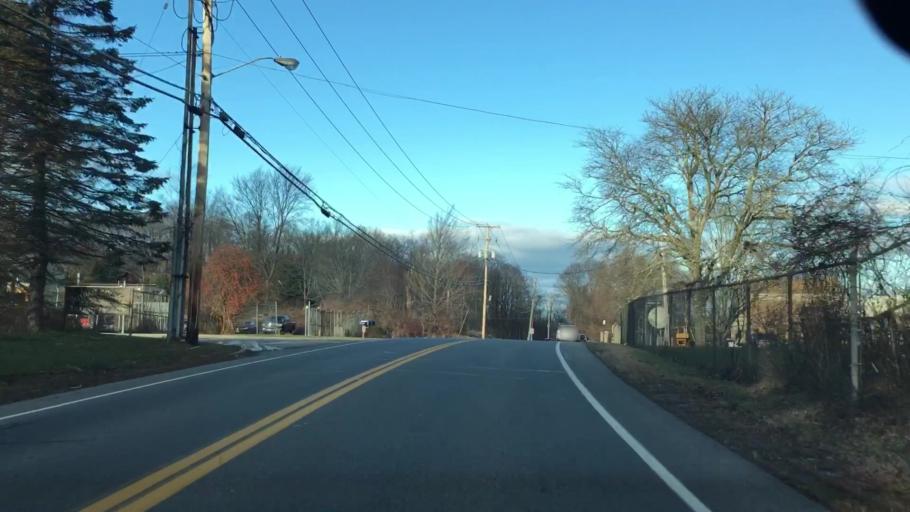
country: US
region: New York
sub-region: Putnam County
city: Lake Carmel
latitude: 41.4704
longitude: -73.6395
